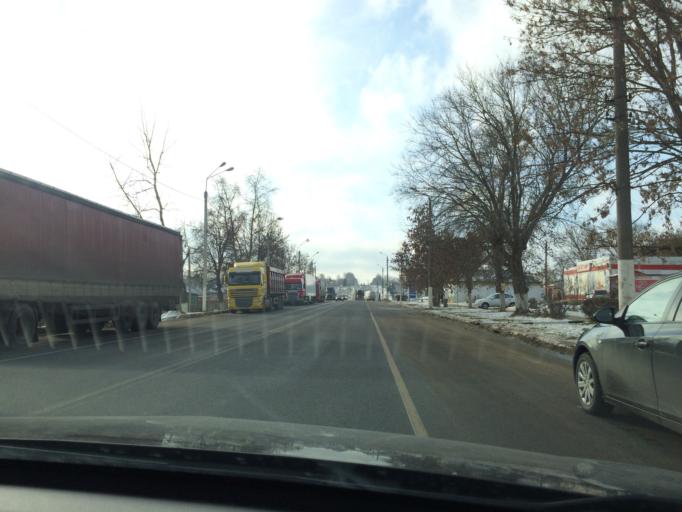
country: RU
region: Tula
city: Plavsk
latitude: 53.7028
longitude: 37.2877
